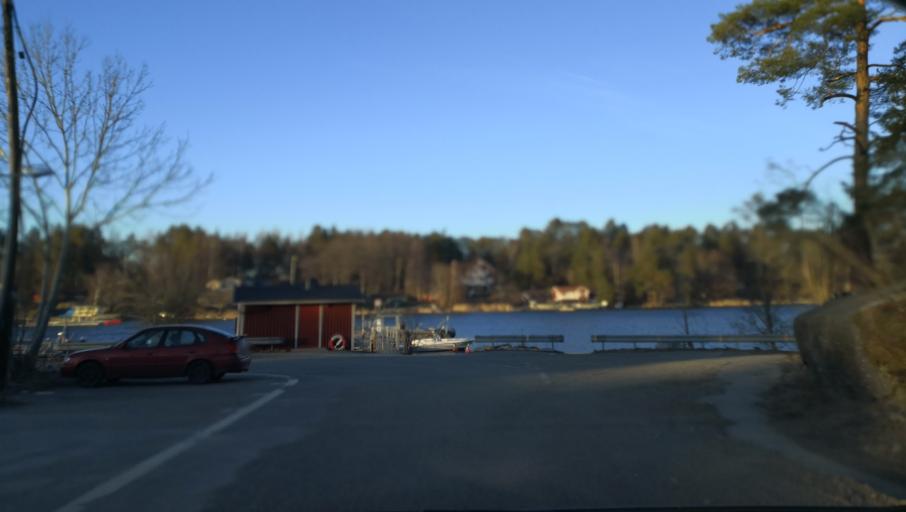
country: SE
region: Stockholm
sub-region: Varmdo Kommun
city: Mortnas
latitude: 59.3381
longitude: 18.4438
